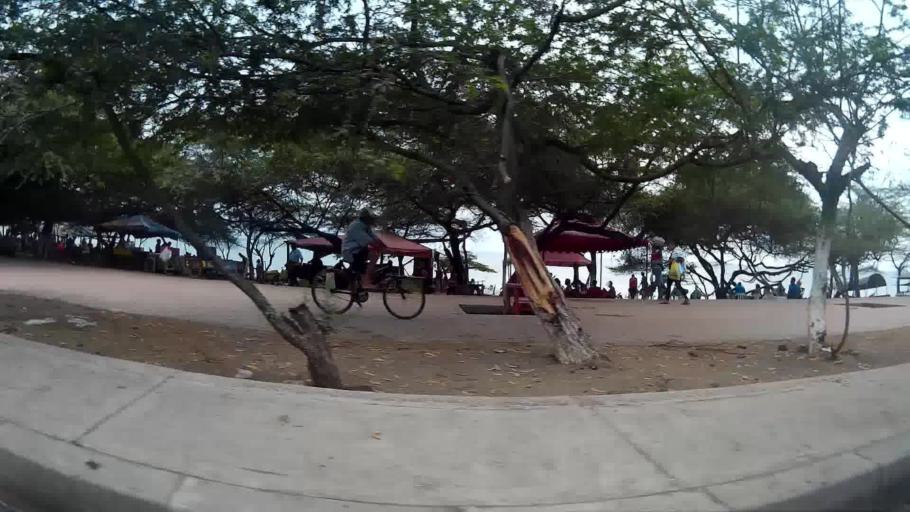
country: CO
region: Magdalena
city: Cienaga
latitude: 11.1220
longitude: -74.2315
